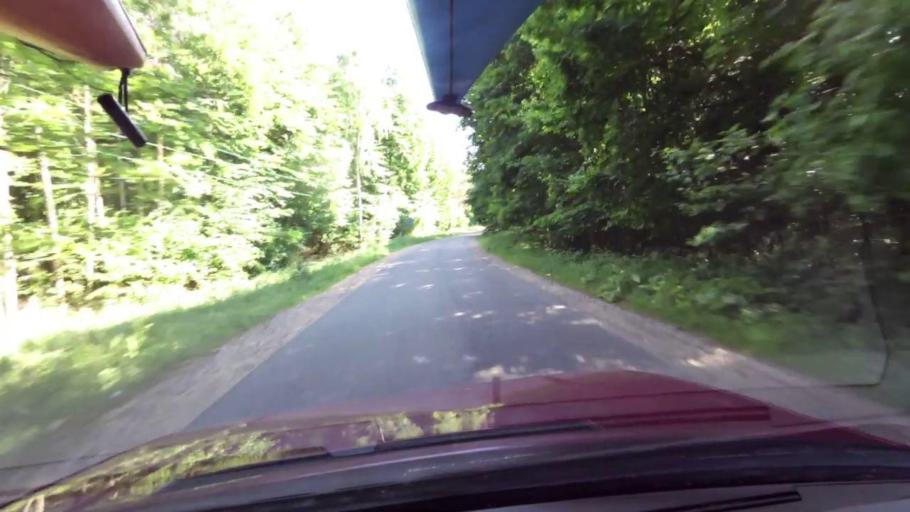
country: PL
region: Pomeranian Voivodeship
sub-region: Powiat slupski
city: Kepice
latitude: 54.1325
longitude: 16.9327
